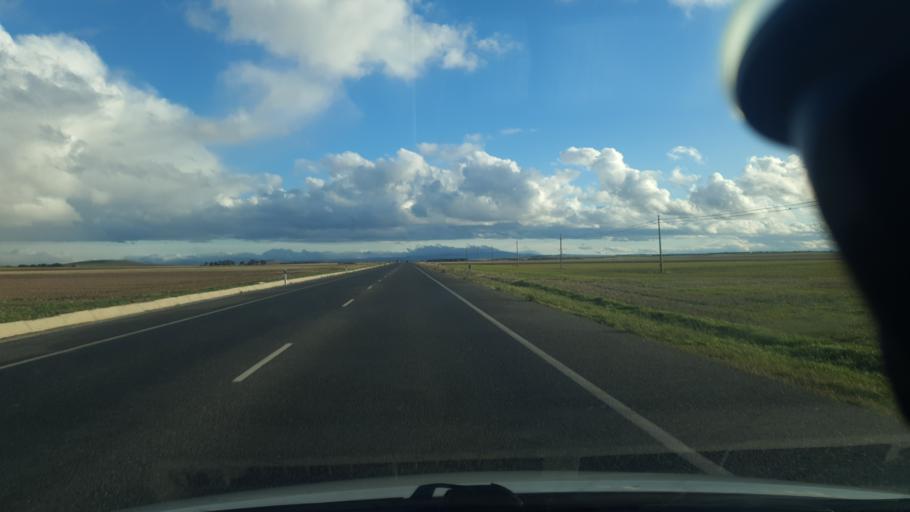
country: ES
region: Castille and Leon
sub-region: Provincia de Segovia
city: Codorniz
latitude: 41.0327
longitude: -4.6190
